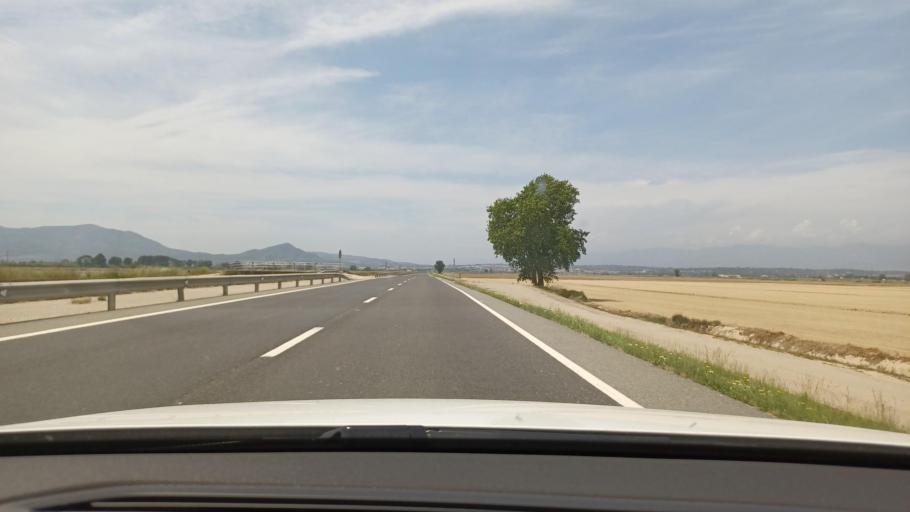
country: ES
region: Catalonia
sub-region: Provincia de Tarragona
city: Amposta
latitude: 40.7161
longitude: 0.6314
